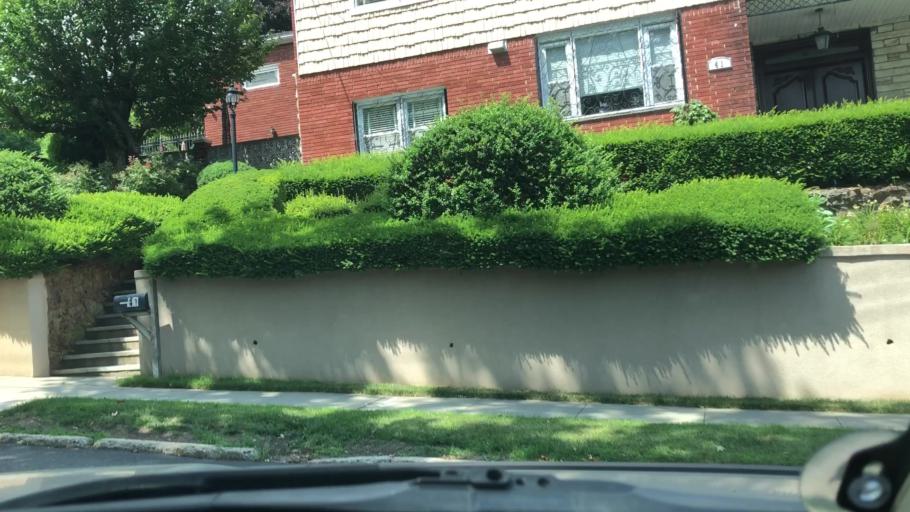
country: US
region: New Jersey
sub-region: Hudson County
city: Bayonne
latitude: 40.6181
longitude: -74.0902
